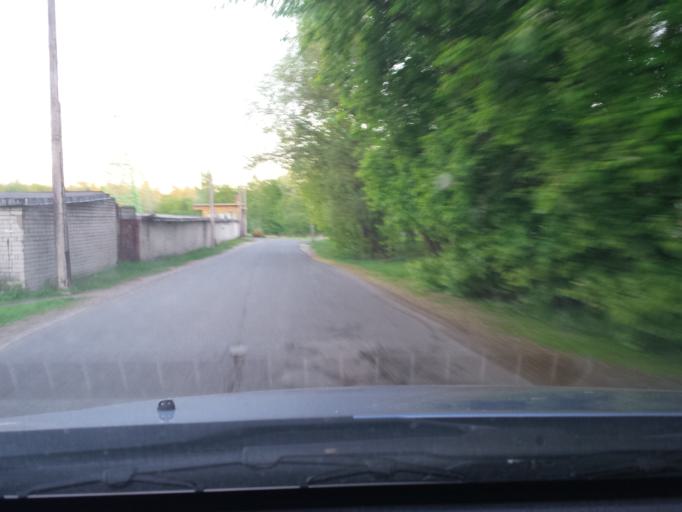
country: LV
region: Riga
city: Riga
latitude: 56.9868
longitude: 24.1371
